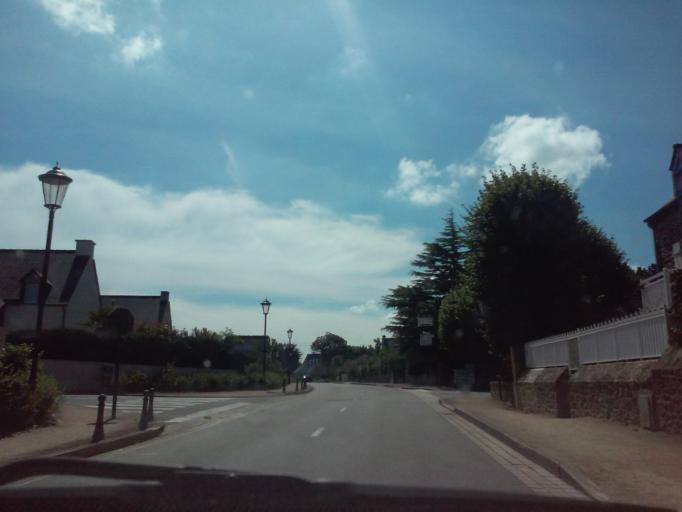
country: FR
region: Brittany
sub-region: Departement d'Ille-et-Vilaine
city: La Richardais
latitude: 48.6203
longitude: -2.0420
